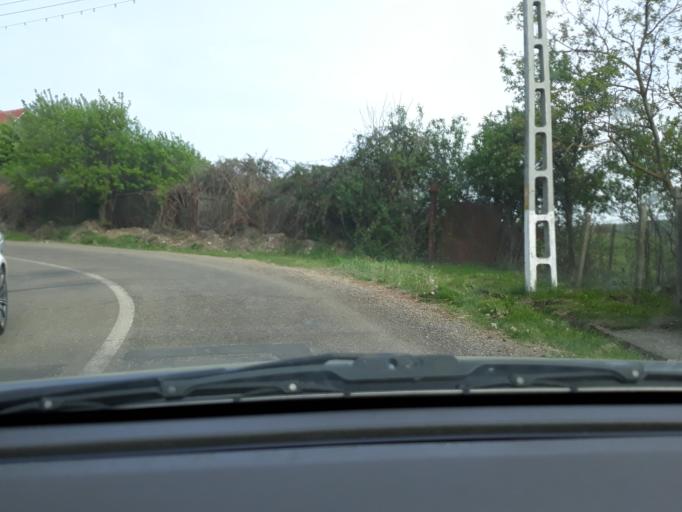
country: RO
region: Bihor
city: Hidiselu de Sus
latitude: 46.9737
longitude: 22.0125
